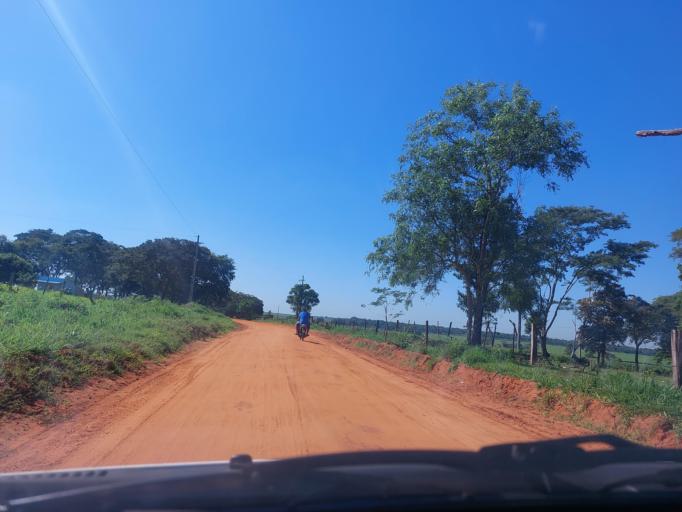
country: PY
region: San Pedro
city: Lima
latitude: -24.1622
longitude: -56.0123
